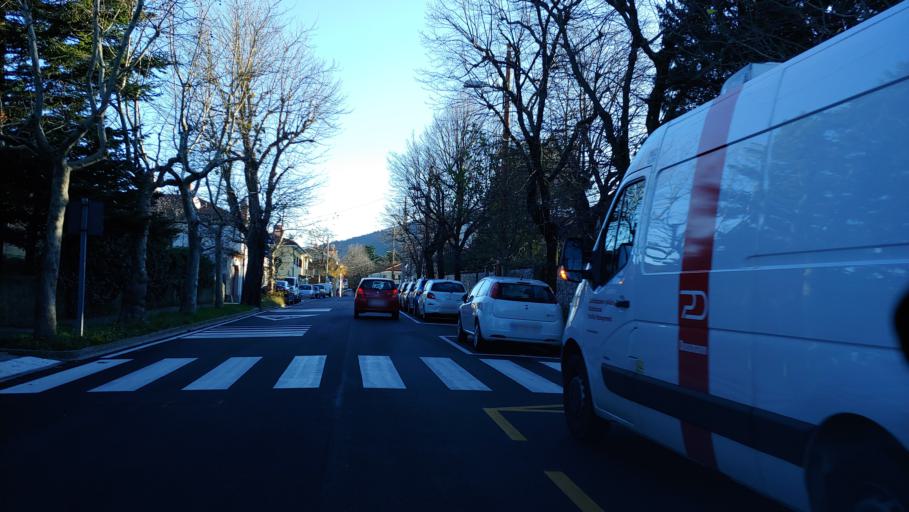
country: IT
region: Friuli Venezia Giulia
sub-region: Provincia di Trieste
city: Dolina
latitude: 45.6409
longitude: 13.8603
